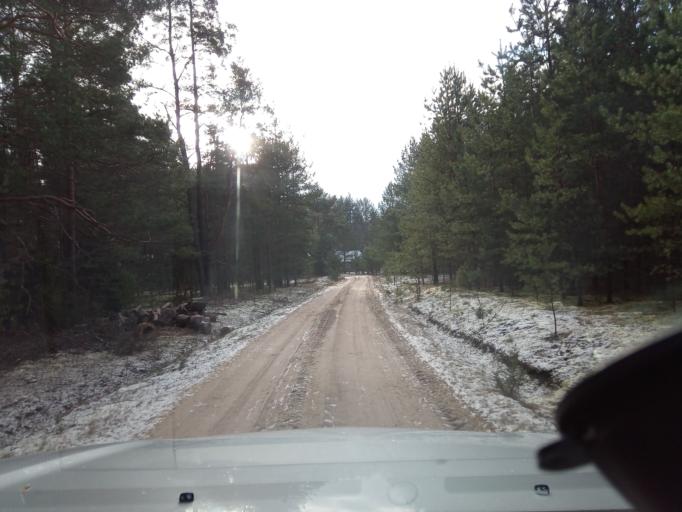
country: LT
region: Alytaus apskritis
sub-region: Alytaus rajonas
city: Daugai
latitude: 54.1115
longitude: 24.2466
